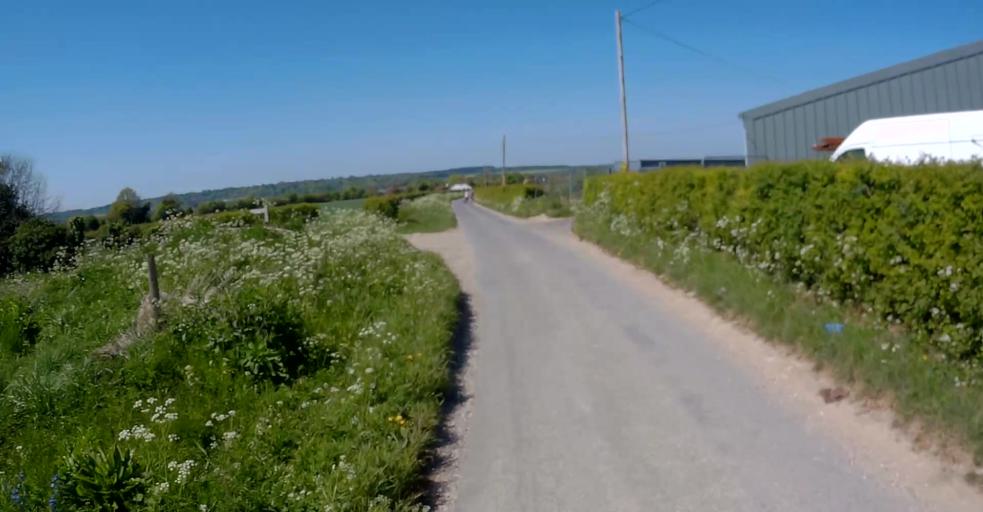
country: GB
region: England
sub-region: Hampshire
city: Overton
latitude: 51.2199
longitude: -1.3230
